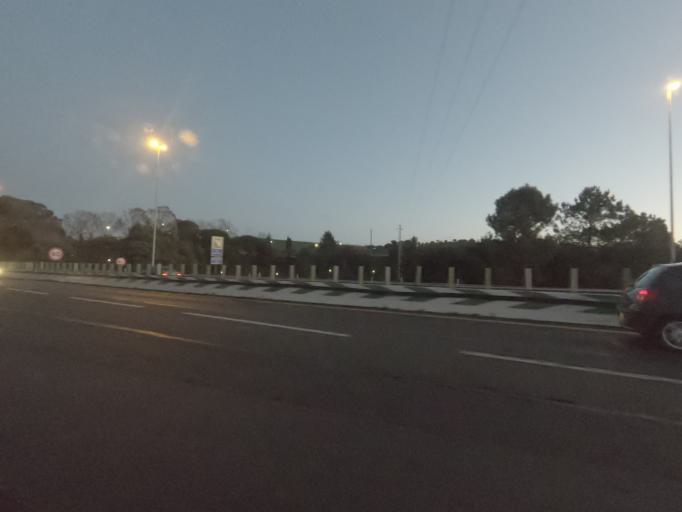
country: PT
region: Porto
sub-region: Gondomar
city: Baguim do Monte
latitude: 41.2011
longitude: -8.5531
